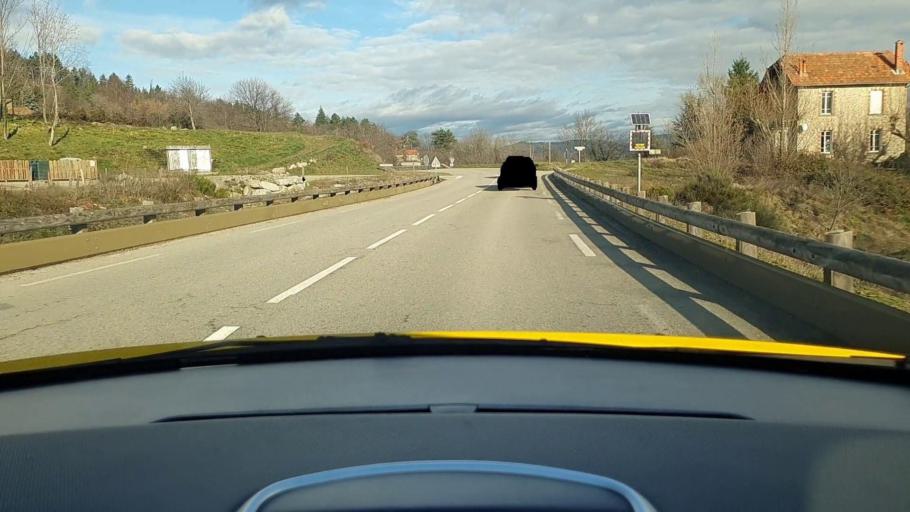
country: FR
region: Languedoc-Roussillon
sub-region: Departement du Gard
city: Branoux-les-Taillades
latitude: 44.3821
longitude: 3.9402
